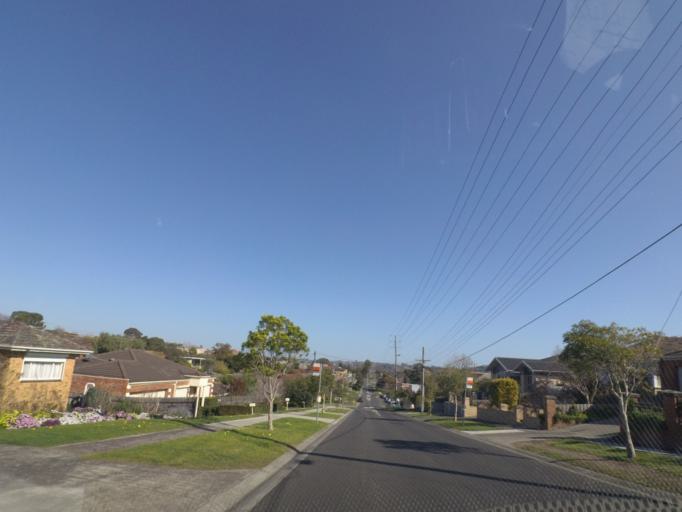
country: AU
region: Victoria
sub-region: Manningham
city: Templestowe Lower
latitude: -37.7753
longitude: 145.1043
